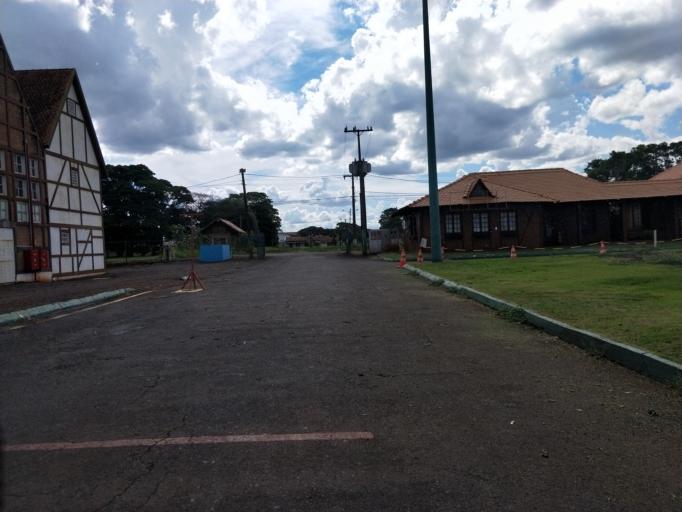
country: BR
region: Parana
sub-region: Marechal Candido Rondon
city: Marechal Candido Rondon
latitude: -24.5529
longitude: -54.0510
